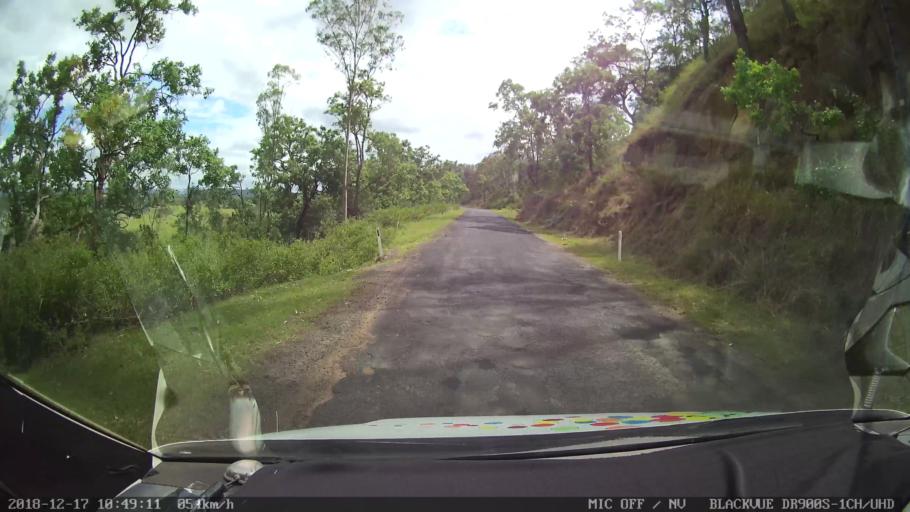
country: AU
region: New South Wales
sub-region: Clarence Valley
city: Gordon
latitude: -28.8676
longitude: 152.5725
